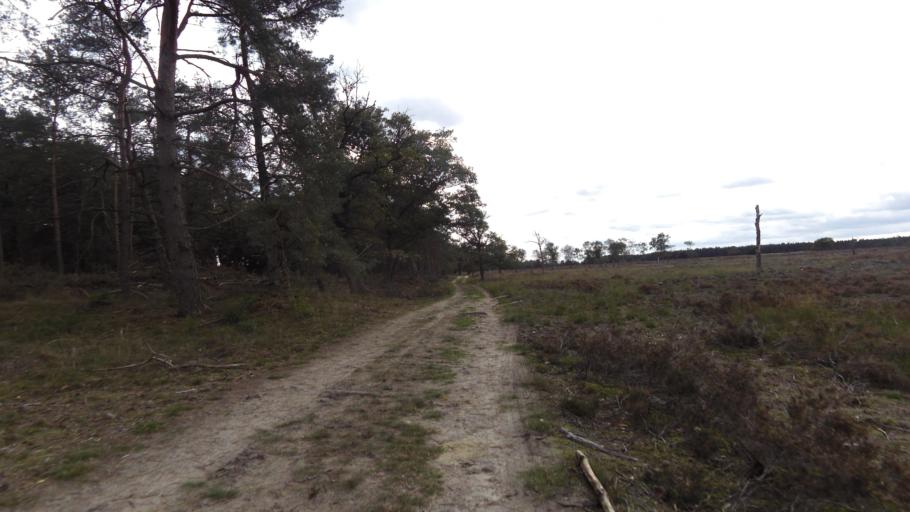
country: NL
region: Gelderland
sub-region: Gemeente Barneveld
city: Stroe
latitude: 52.1800
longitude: 5.7262
